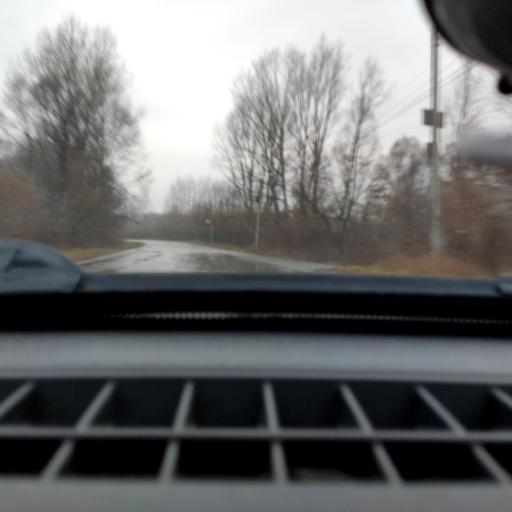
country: RU
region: Bashkortostan
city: Iglino
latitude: 54.8079
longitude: 56.1892
